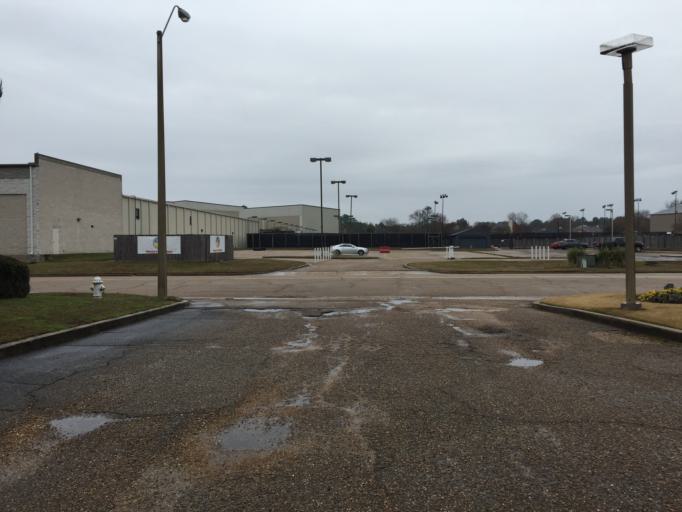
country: US
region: Mississippi
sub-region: Madison County
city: Ridgeland
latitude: 32.3856
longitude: -90.1118
